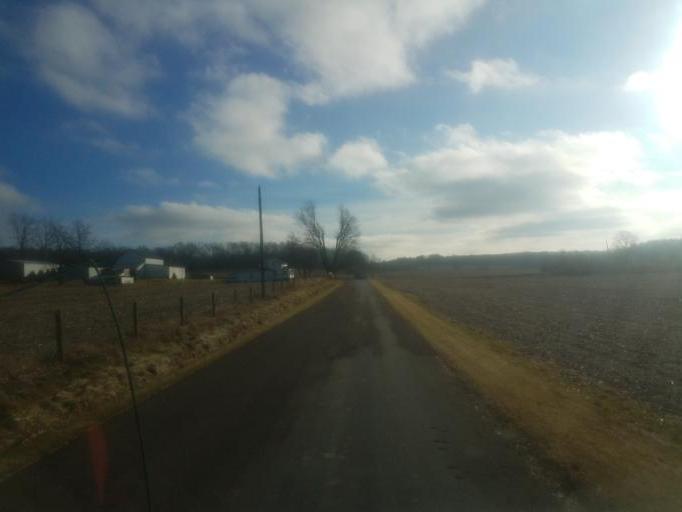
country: US
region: Ohio
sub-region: Ashland County
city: Loudonville
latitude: 40.5817
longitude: -82.3568
